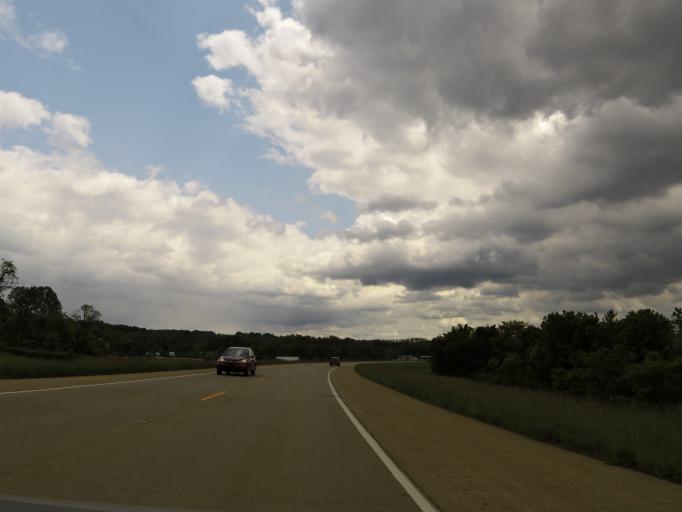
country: US
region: West Virginia
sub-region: Jackson County
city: Ravenswood
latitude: 38.9540
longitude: -81.8056
